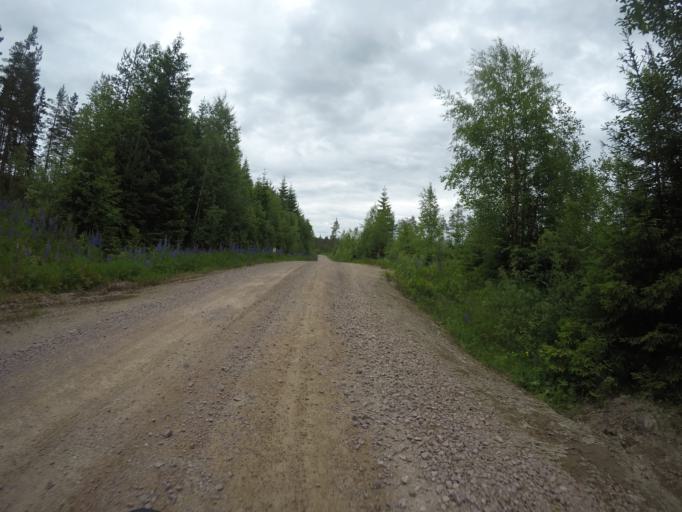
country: SE
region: Dalarna
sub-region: Ludvika Kommun
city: Abborrberget
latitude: 60.1009
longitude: 14.5325
